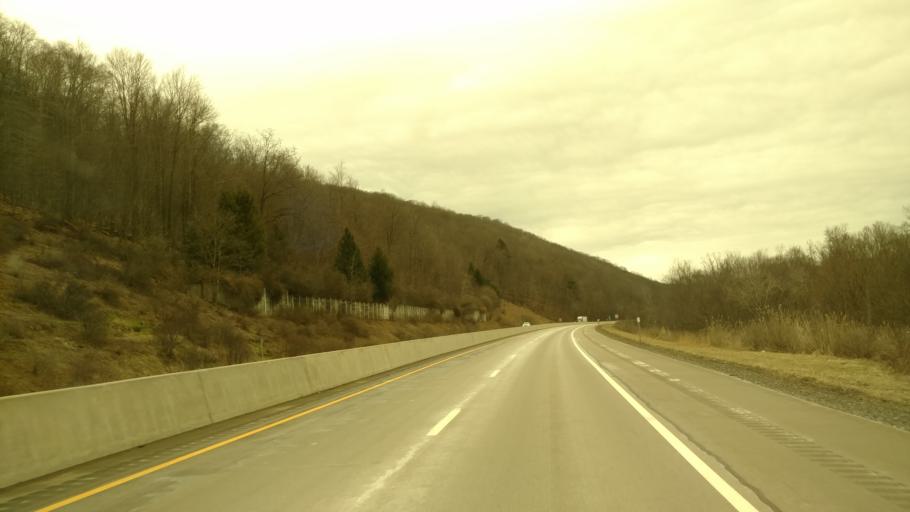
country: US
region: New York
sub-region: Cattaraugus County
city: Salamanca
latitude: 42.1256
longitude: -78.6661
